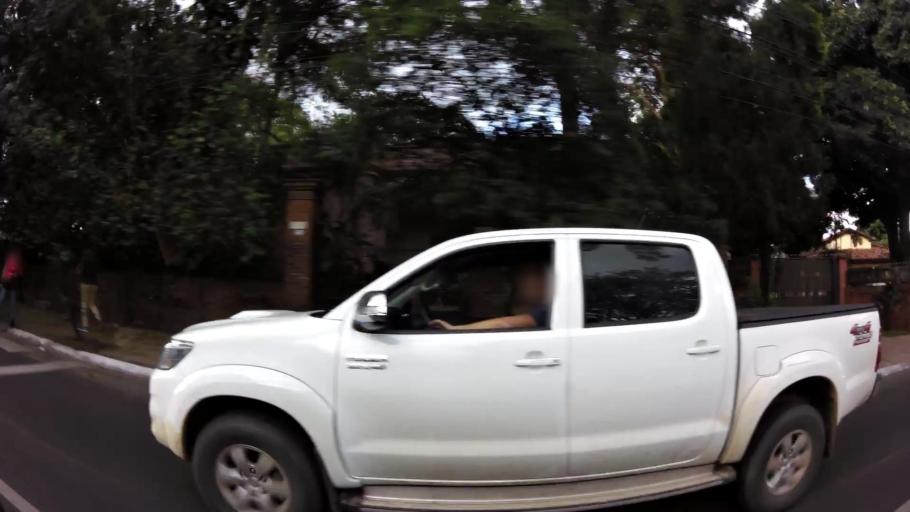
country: PY
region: Asuncion
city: Asuncion
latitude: -25.2917
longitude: -57.5991
